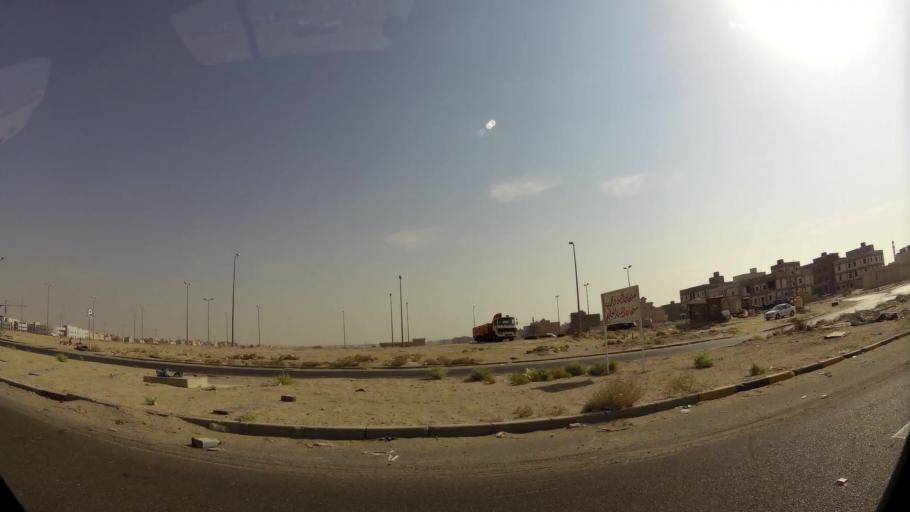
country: KW
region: Al Ahmadi
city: Al Wafrah
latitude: 28.7757
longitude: 48.0520
